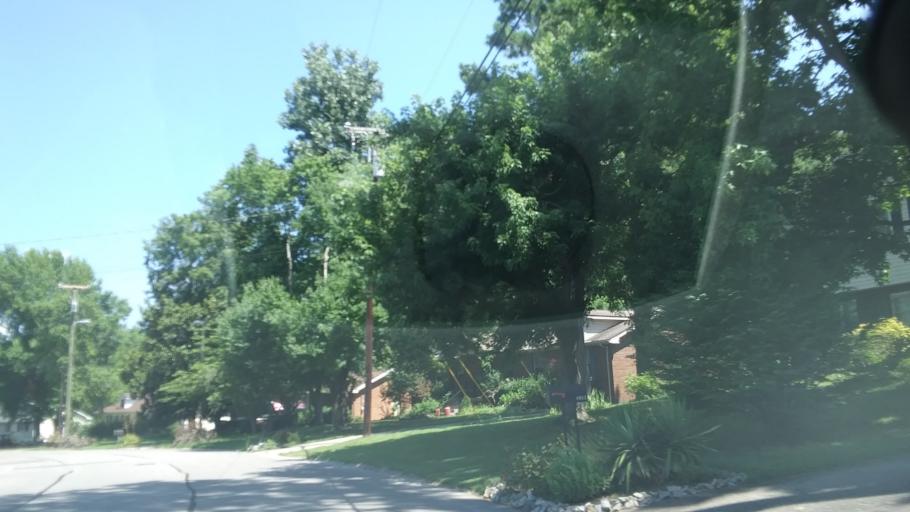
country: US
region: Tennessee
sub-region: Davidson County
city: Belle Meade
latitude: 36.0821
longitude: -86.9392
